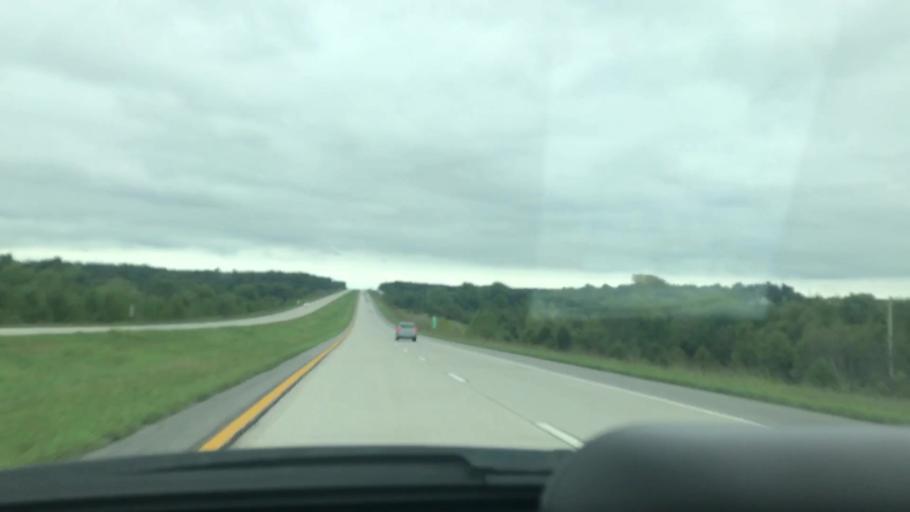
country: US
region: Missouri
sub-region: Greene County
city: Fair Grove
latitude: 37.4645
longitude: -93.1392
